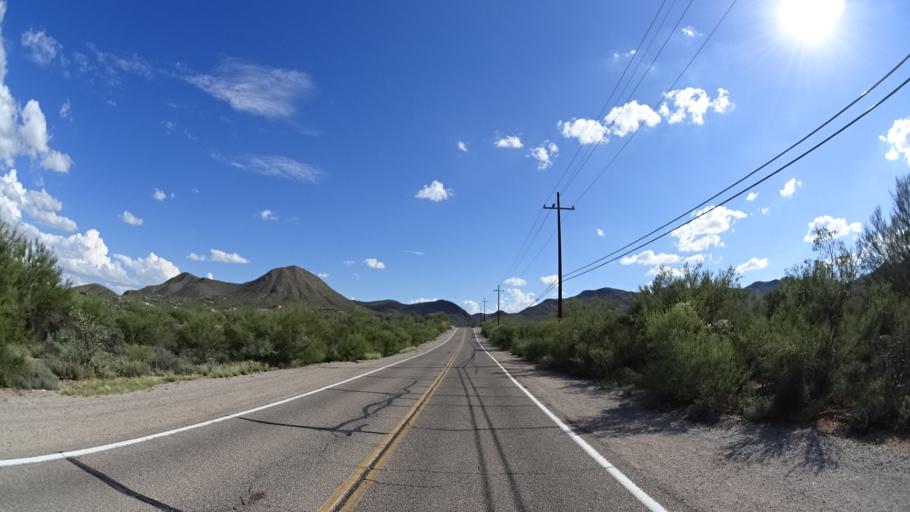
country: US
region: Arizona
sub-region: Pima County
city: Tucson Estates
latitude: 32.2406
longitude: -111.0628
